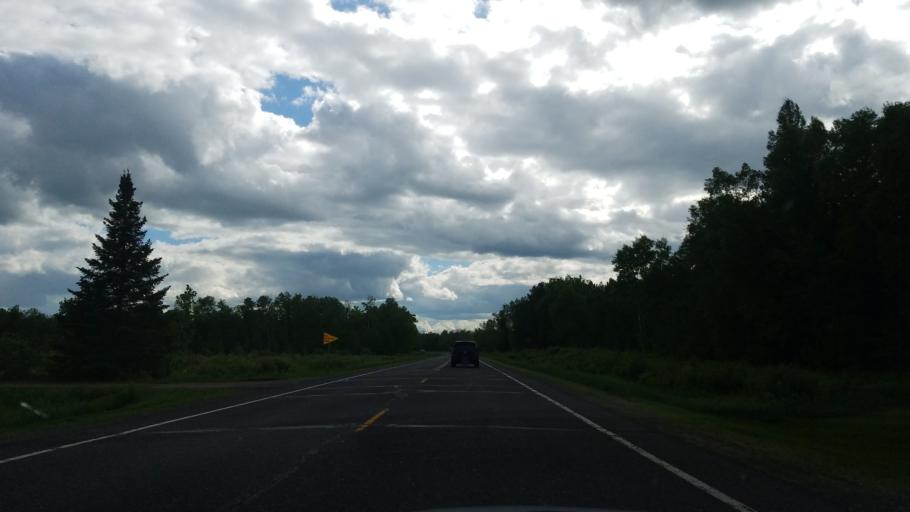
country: US
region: Wisconsin
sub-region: Burnett County
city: Siren
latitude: 46.1697
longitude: -92.2303
